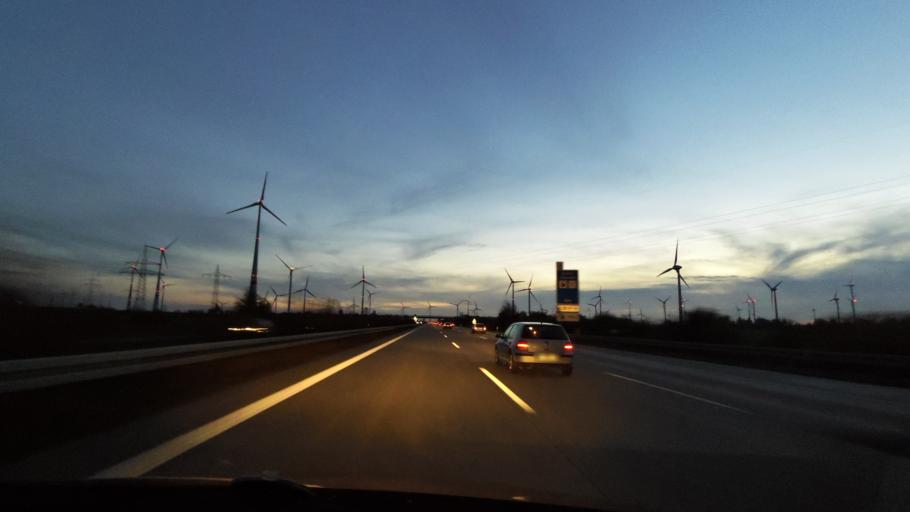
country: DE
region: Saxony-Anhalt
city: Nessa
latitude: 51.1467
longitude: 11.9775
